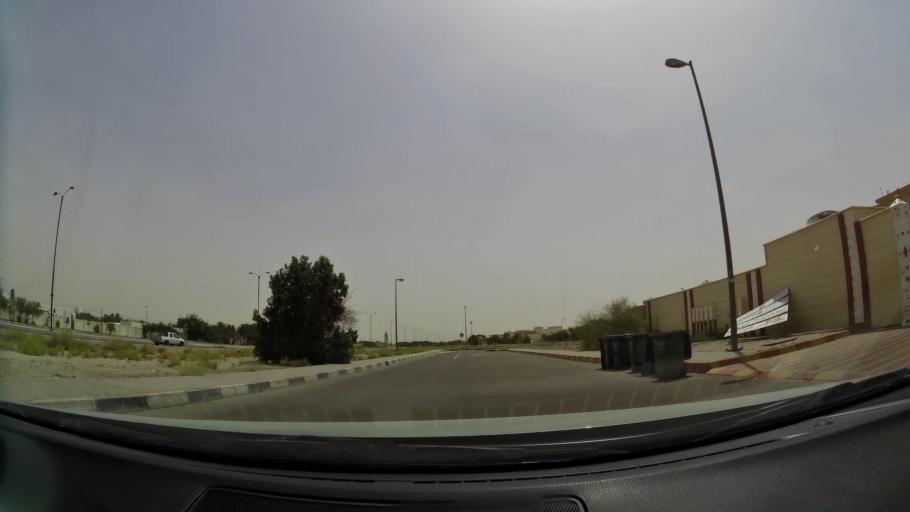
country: AE
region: Abu Dhabi
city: Al Ain
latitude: 24.1396
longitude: 55.6385
